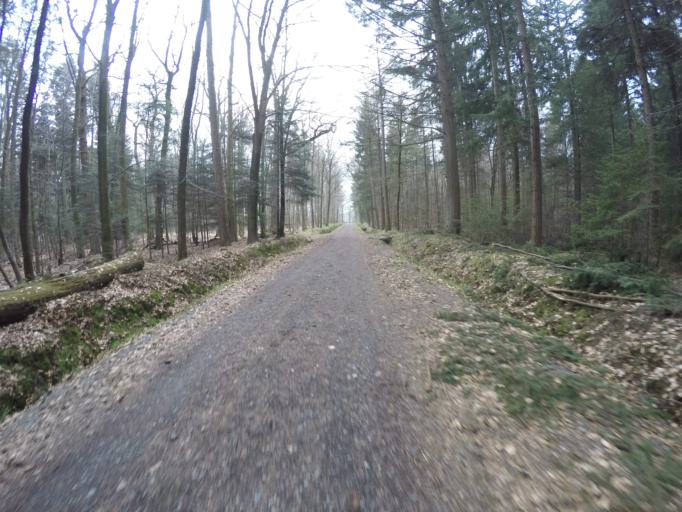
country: DE
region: Schleswig-Holstein
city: Borstel-Hohenraden
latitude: 53.7210
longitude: 9.8098
